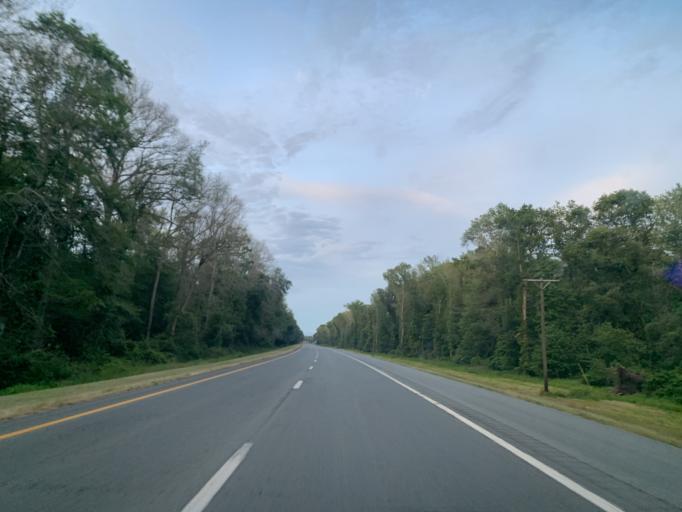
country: US
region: Maryland
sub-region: Wicomico County
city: Pittsville
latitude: 38.3841
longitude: -75.3337
